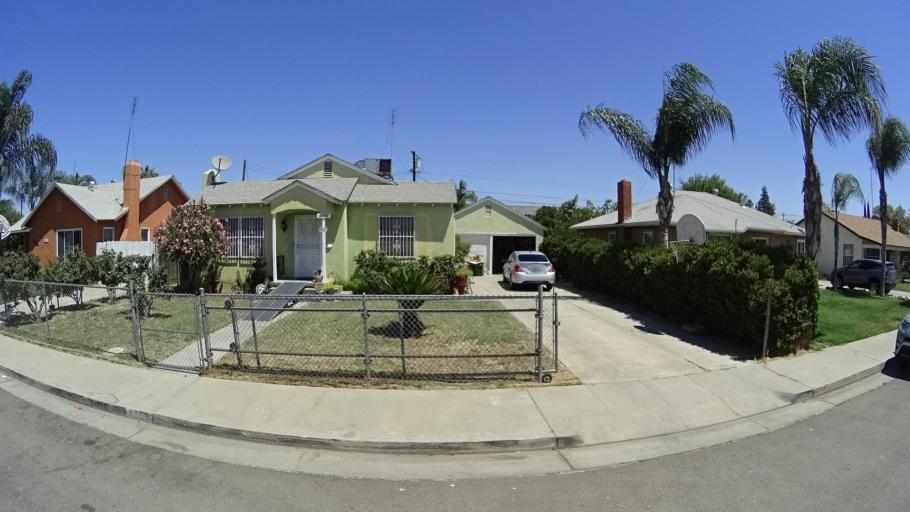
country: US
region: California
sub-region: Fresno County
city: Fresno
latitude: 36.7416
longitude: -119.7411
